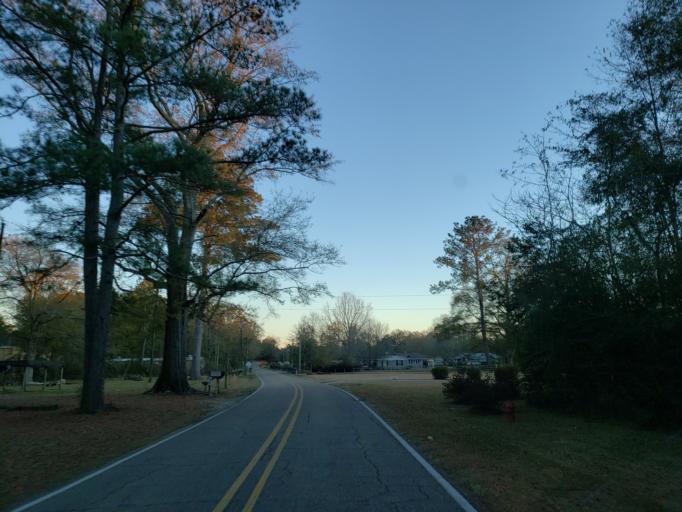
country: US
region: Mississippi
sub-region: Forrest County
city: Glendale
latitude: 31.3760
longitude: -89.3356
